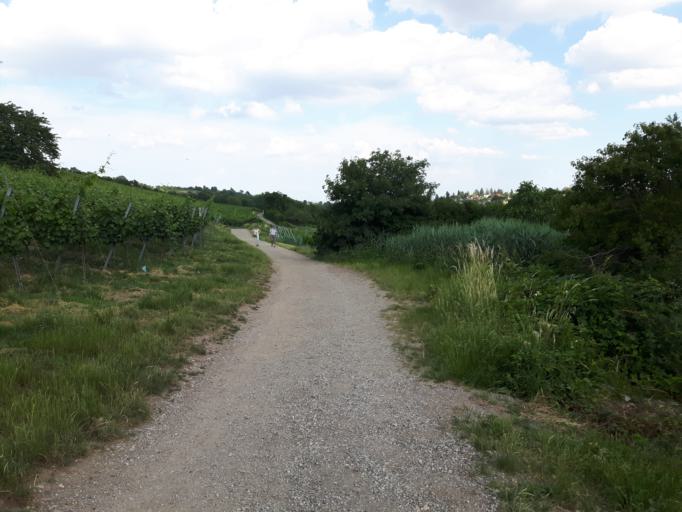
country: AT
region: Lower Austria
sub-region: Politischer Bezirk Wien-Umgebung
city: Klosterneuburg
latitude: 48.2551
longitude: 16.3042
